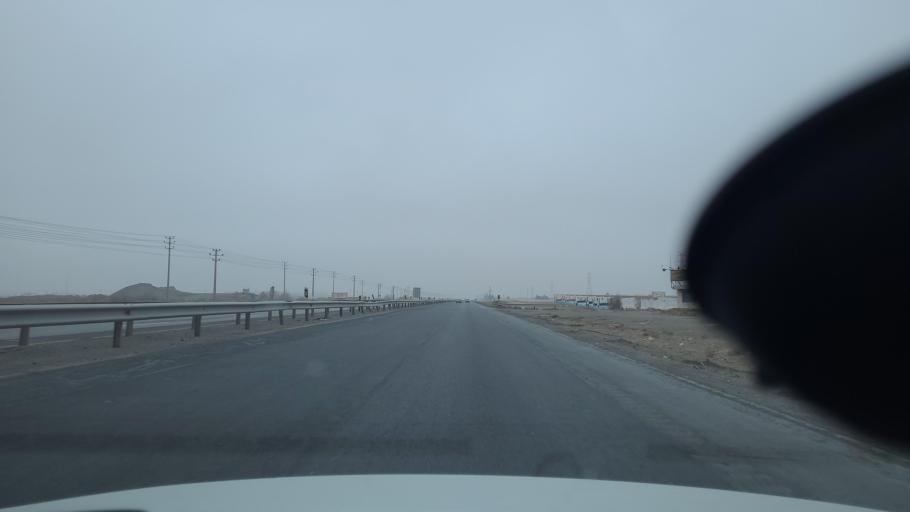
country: IR
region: Razavi Khorasan
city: Fariman
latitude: 35.9332
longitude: 59.7517
